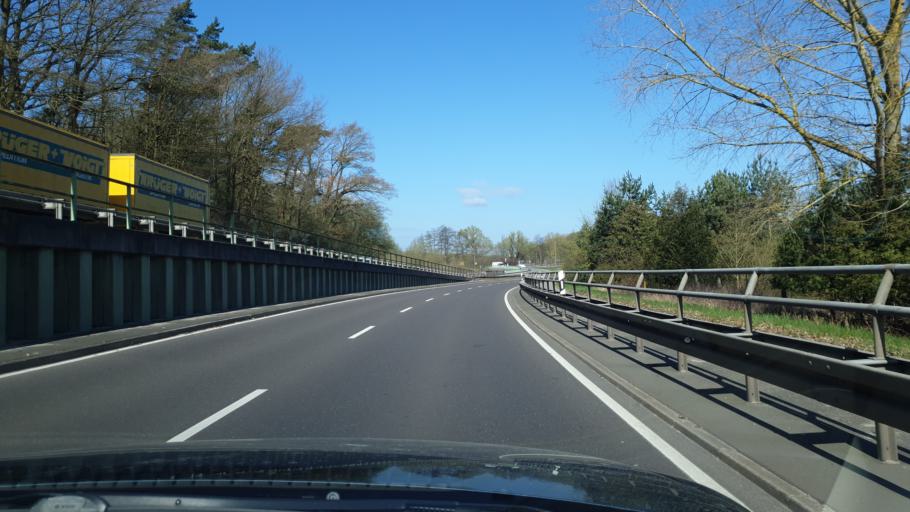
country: DE
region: Mecklenburg-Vorpommern
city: Neumuehle
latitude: 53.6226
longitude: 11.3639
